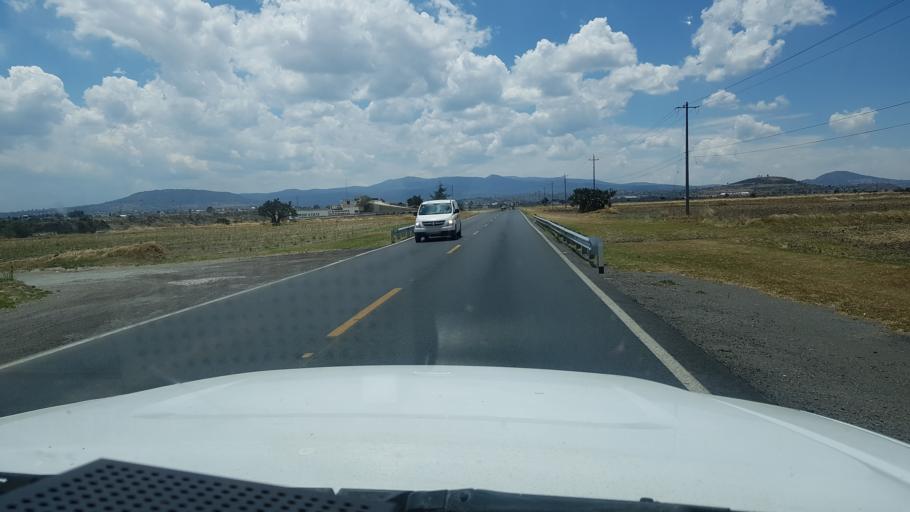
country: MX
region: Hidalgo
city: Calpulalpan
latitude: 19.6102
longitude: -98.5589
